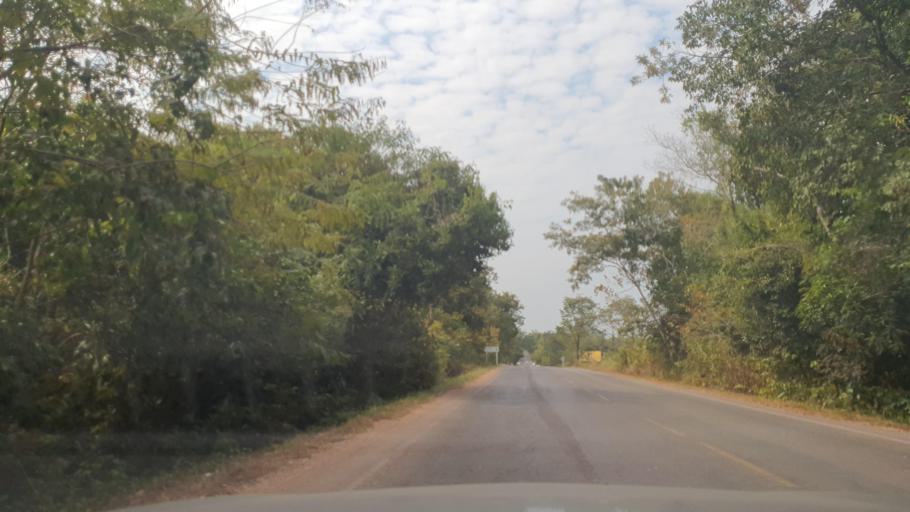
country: TH
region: Changwat Bueng Kan
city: Bung Khla
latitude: 18.2978
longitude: 103.9387
